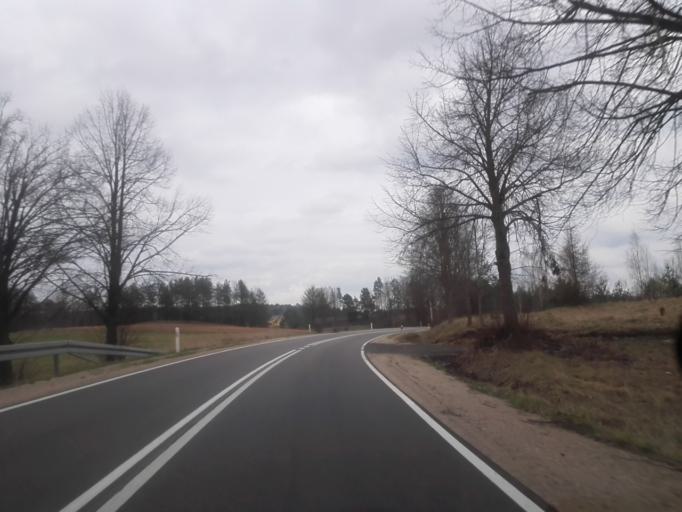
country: PL
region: Podlasie
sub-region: Powiat sejnenski
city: Sejny
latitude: 54.0674
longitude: 23.3570
